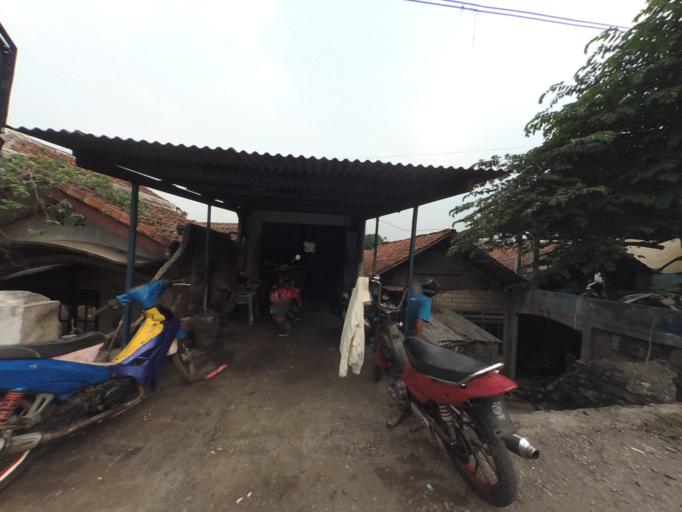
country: ID
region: West Java
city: Ciampea
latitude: -6.5604
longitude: 106.6856
